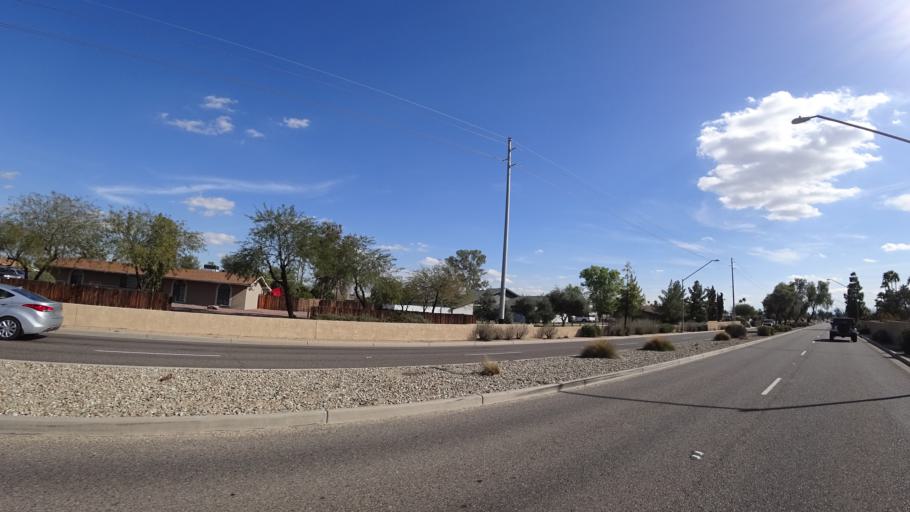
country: US
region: Arizona
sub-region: Maricopa County
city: Peoria
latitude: 33.6502
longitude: -112.2205
